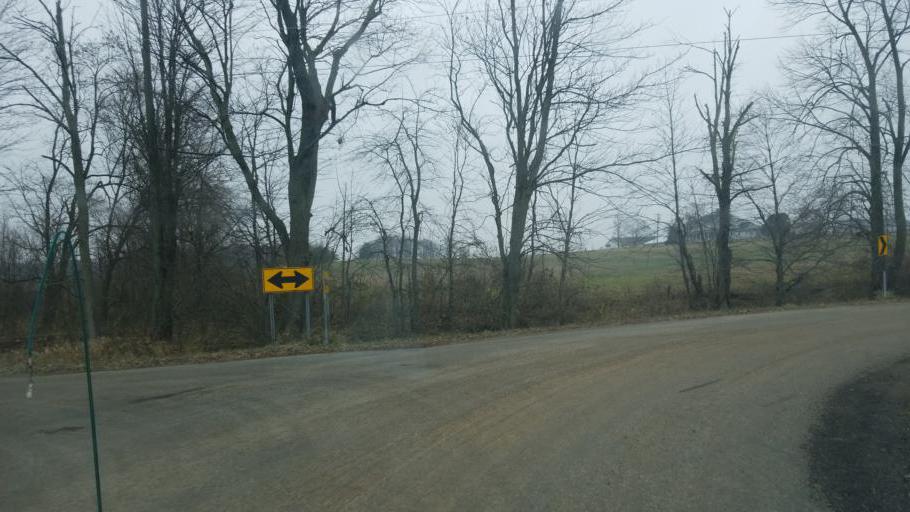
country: US
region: Ohio
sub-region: Huron County
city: New London
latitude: 41.0160
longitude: -82.3549
